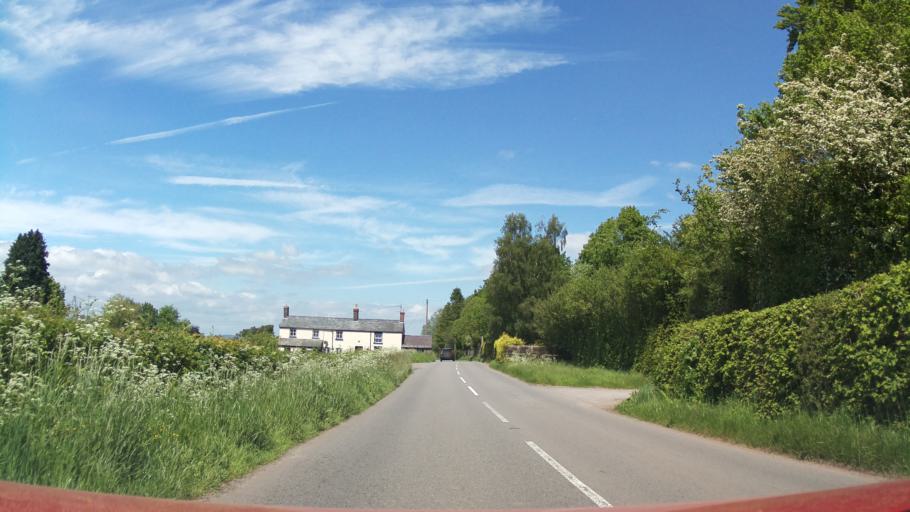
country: GB
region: Wales
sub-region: Monmouthshire
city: Llangwm
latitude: 51.7159
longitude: -2.7630
